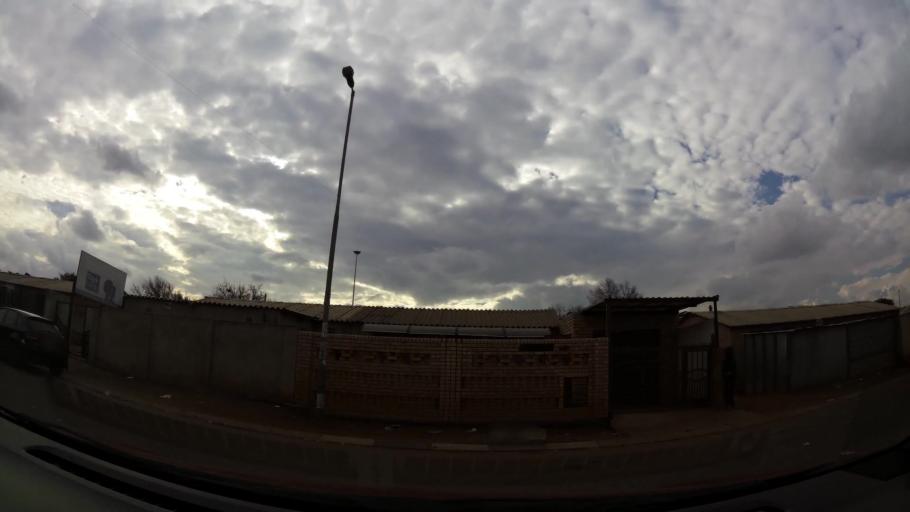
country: ZA
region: Gauteng
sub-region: City of Johannesburg Metropolitan Municipality
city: Soweto
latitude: -26.2423
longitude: 27.8389
